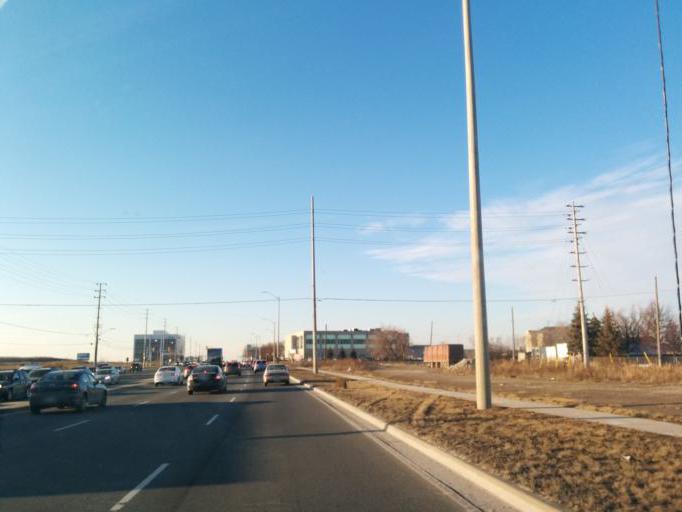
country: CA
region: Ontario
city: Mississauga
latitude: 43.6320
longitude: -79.6871
